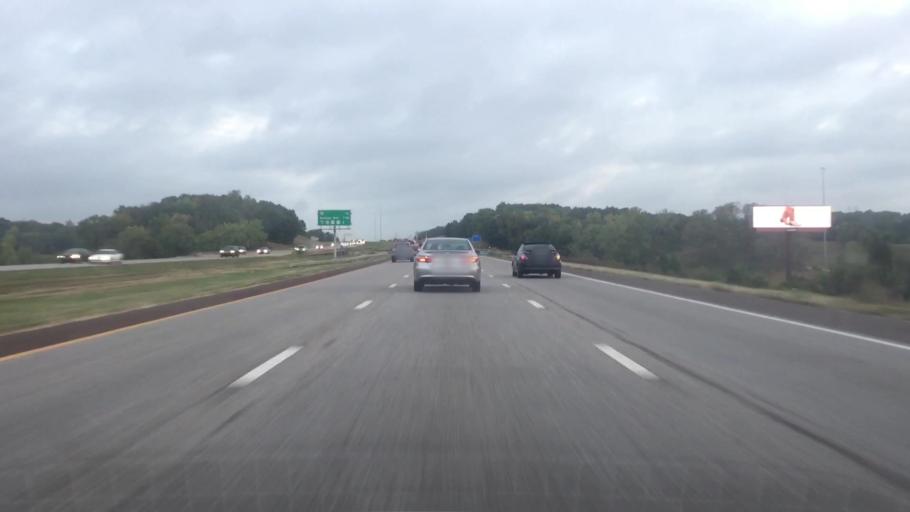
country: US
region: Kansas
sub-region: Wyandotte County
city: Edwardsville
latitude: 39.0600
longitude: -94.7912
